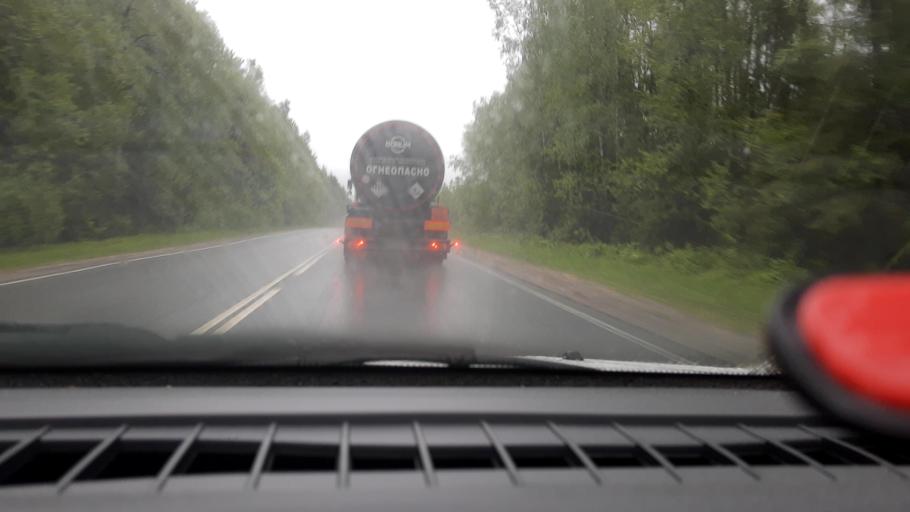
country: RU
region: Nizjnij Novgorod
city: Vladimirskoye
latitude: 56.8781
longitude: 44.9643
